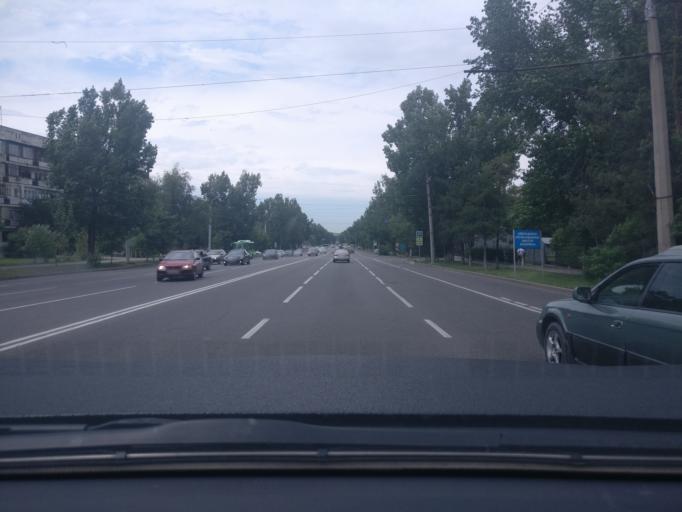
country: KZ
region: Almaty Qalasy
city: Almaty
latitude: 43.2410
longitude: 76.8584
